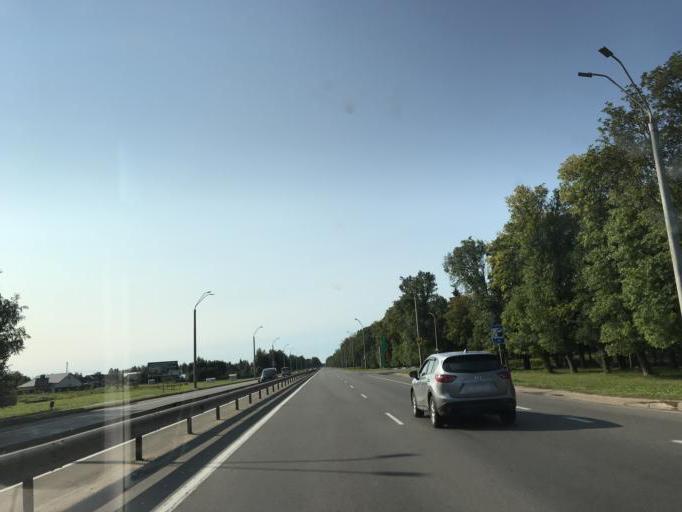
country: BY
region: Mogilev
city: Buynichy
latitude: 53.8587
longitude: 30.2568
